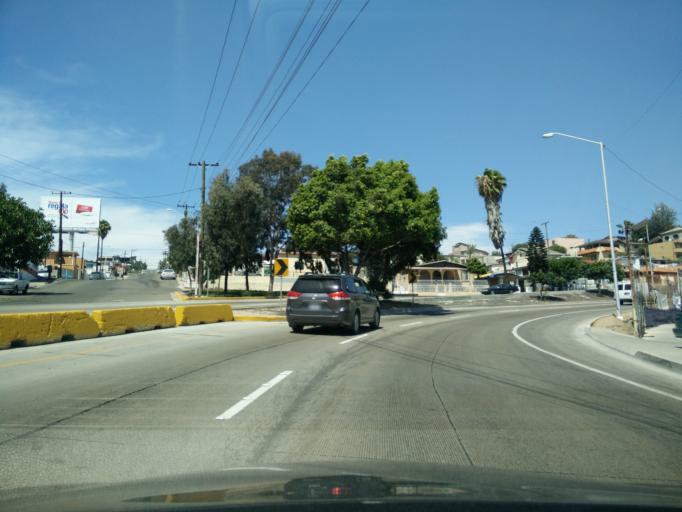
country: MX
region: Baja California
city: Tijuana
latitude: 32.5348
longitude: -117.0075
